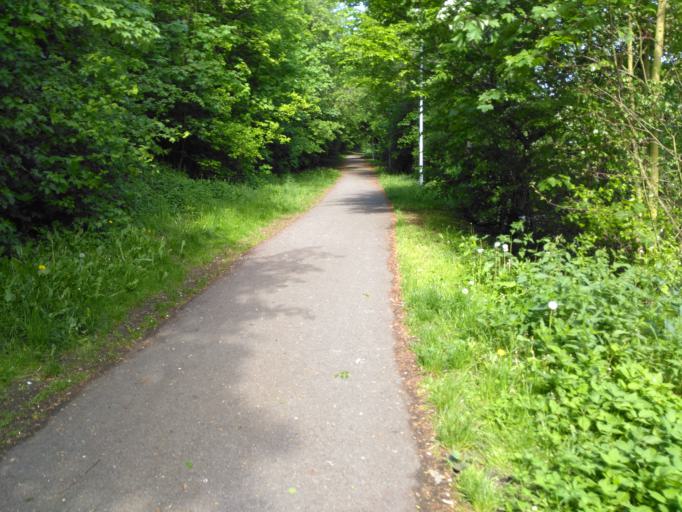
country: CZ
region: Central Bohemia
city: Cernosice
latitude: 49.9867
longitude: 14.3537
